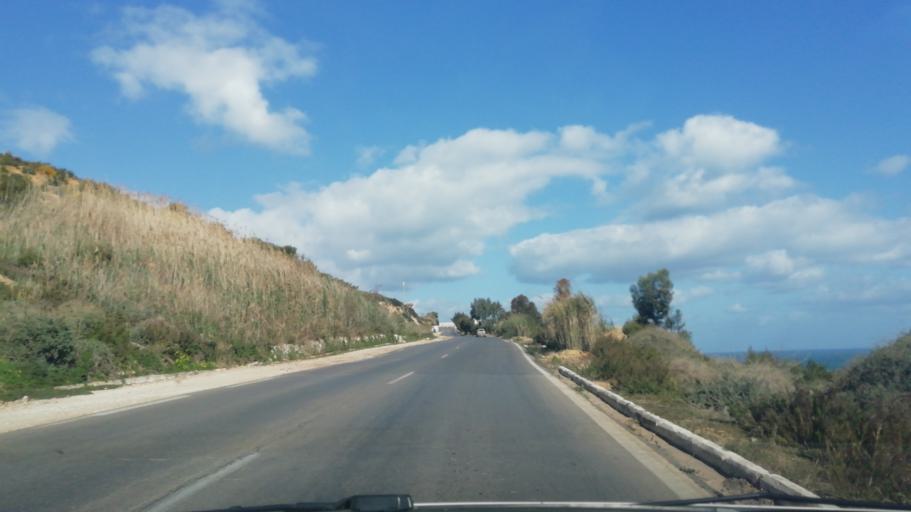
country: DZ
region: Relizane
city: Mazouna
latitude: 36.3193
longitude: 0.6801
